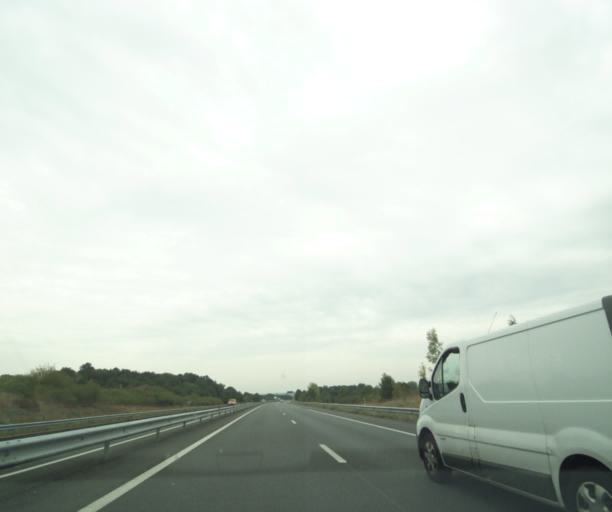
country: FR
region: Pays de la Loire
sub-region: Departement de la Vendee
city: Les Essarts
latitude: 46.7731
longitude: -1.1838
